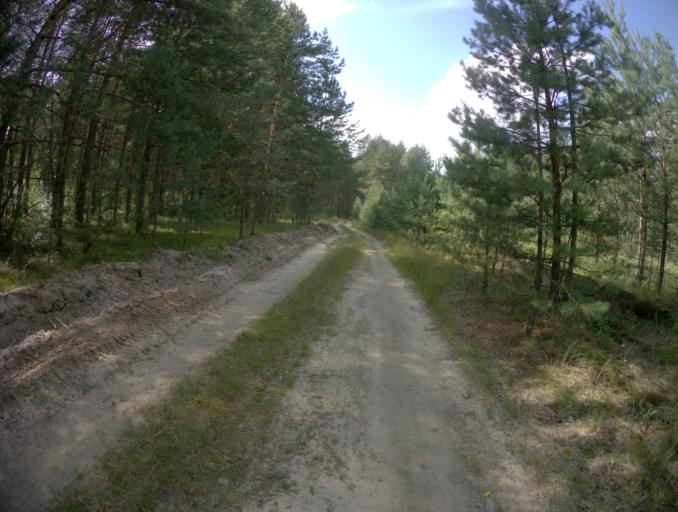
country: RU
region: Vladimir
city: Vorsha
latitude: 55.9664
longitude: 40.1821
